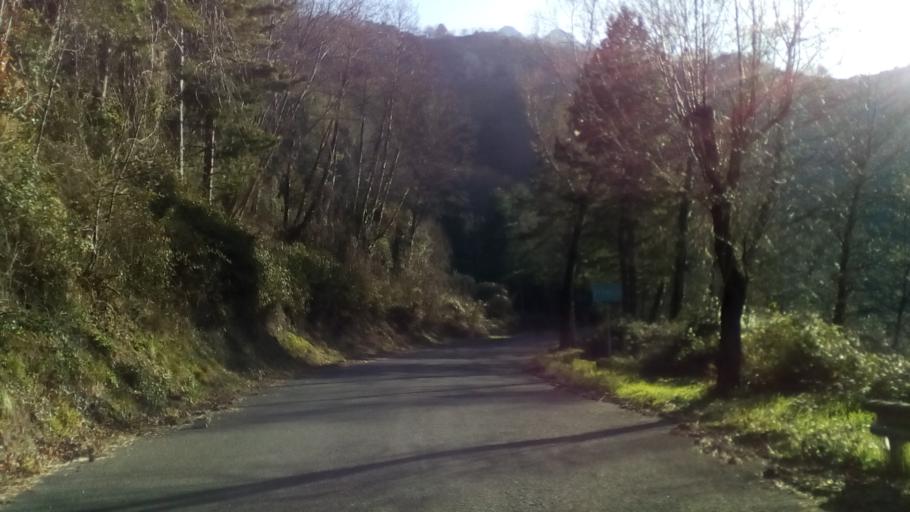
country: IT
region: Tuscany
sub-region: Provincia di Massa-Carrara
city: Montignoso
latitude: 44.0554
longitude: 10.2014
